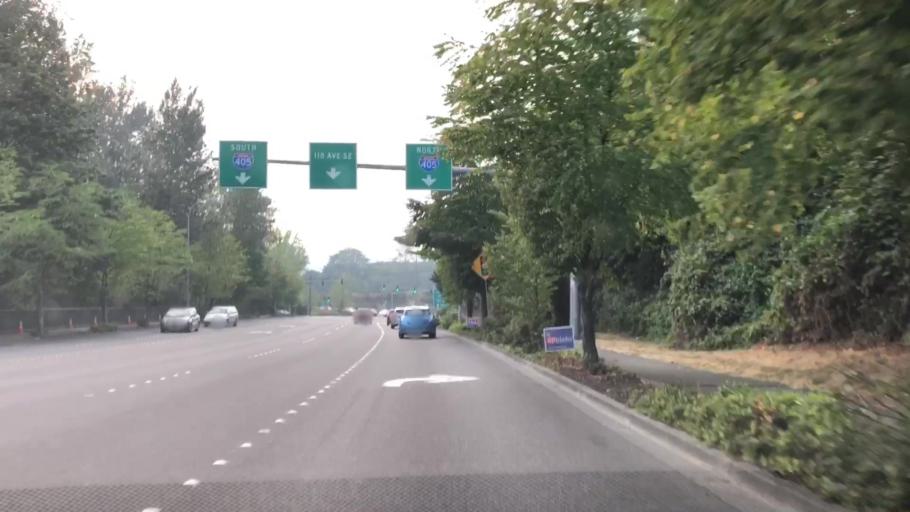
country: US
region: Washington
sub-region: King County
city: Newport
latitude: 47.5668
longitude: -122.1768
